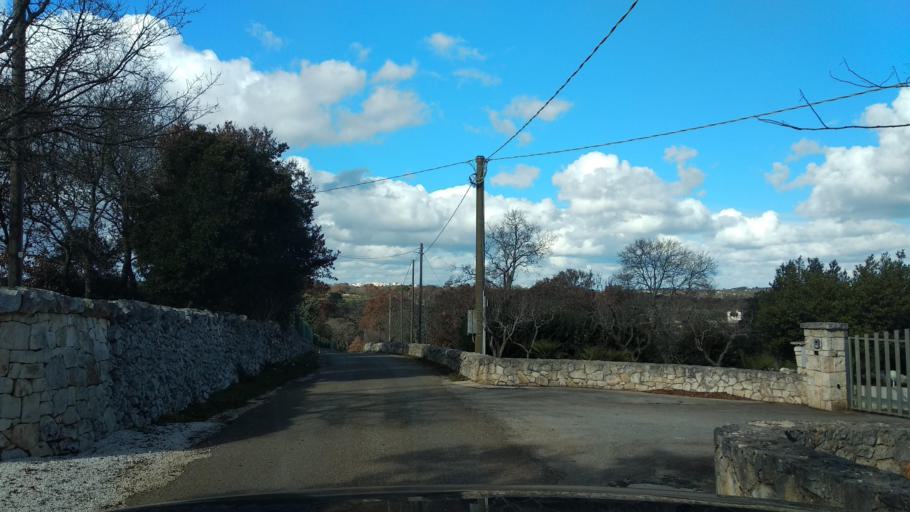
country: IT
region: Apulia
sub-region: Provincia di Brindisi
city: Casalini
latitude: 40.7113
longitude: 17.4537
